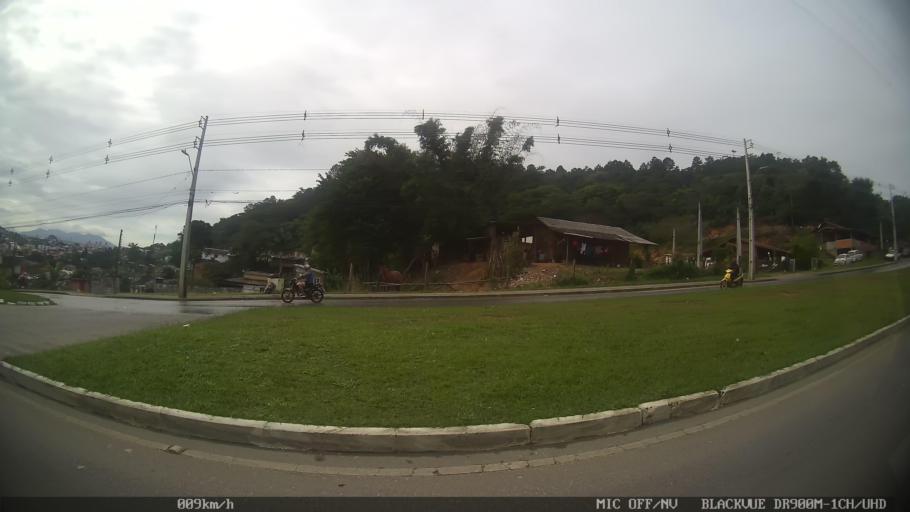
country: BR
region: Santa Catarina
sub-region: Sao Jose
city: Campinas
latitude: -27.5525
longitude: -48.6446
